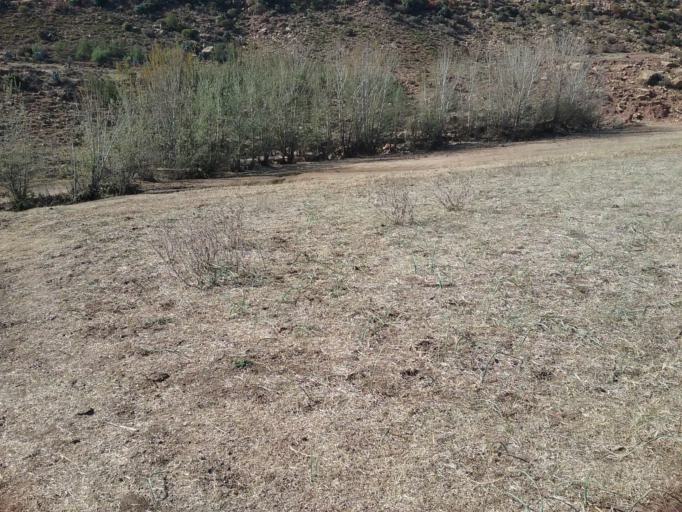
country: LS
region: Maseru
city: Nako
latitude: -29.4794
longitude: 27.6448
